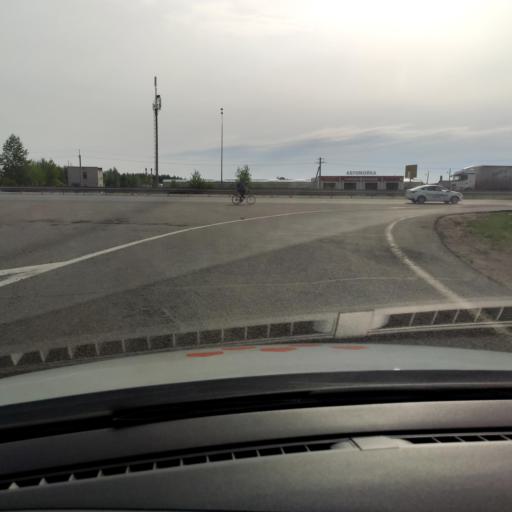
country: RU
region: Tatarstan
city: Vysokaya Gora
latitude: 55.7443
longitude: 49.3994
